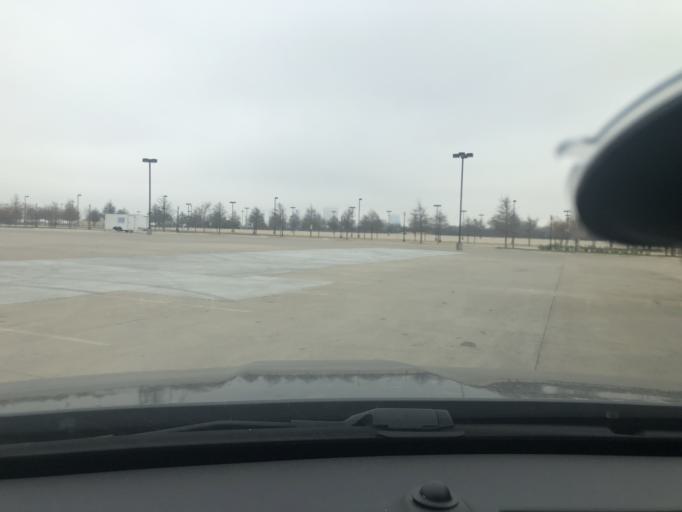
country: US
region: Texas
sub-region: Tarrant County
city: Westworth
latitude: 32.7381
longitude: -97.3689
